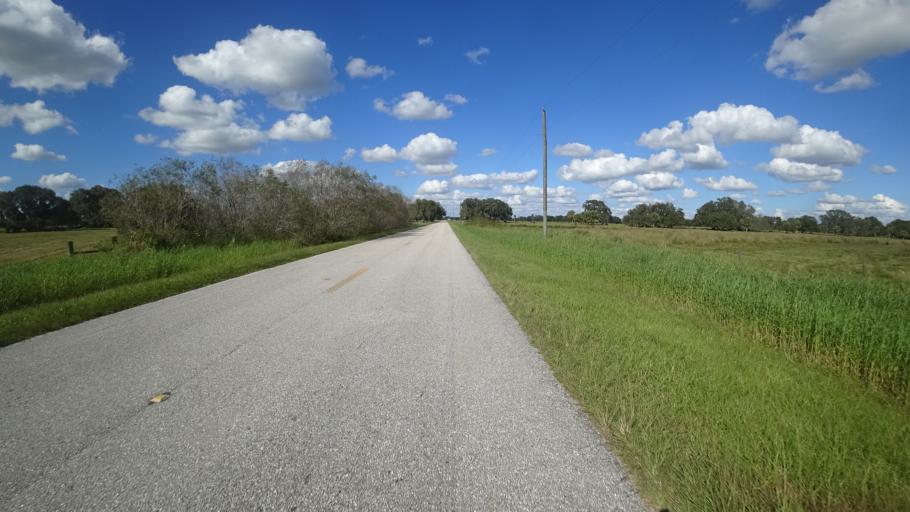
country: US
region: Florida
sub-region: Sarasota County
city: North Port
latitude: 27.1943
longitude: -82.1223
